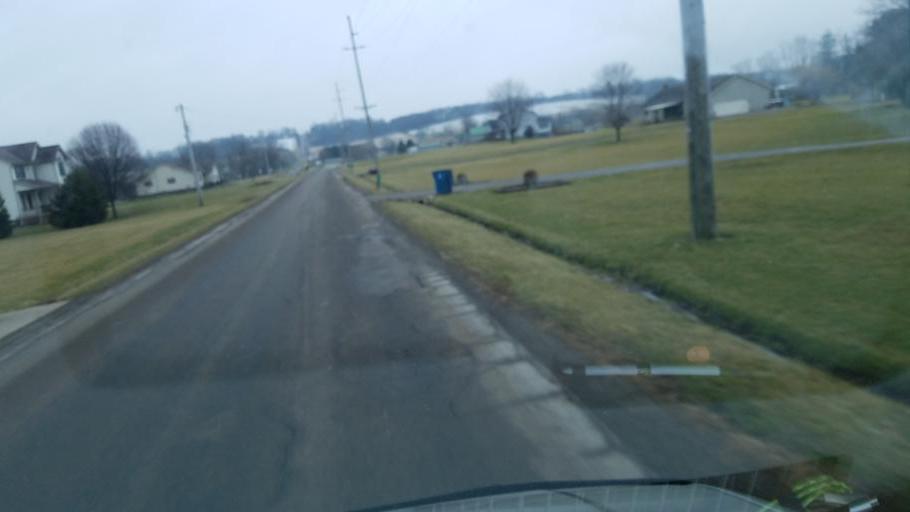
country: US
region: Ohio
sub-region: Wayne County
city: Apple Creek
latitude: 40.7111
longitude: -81.8800
